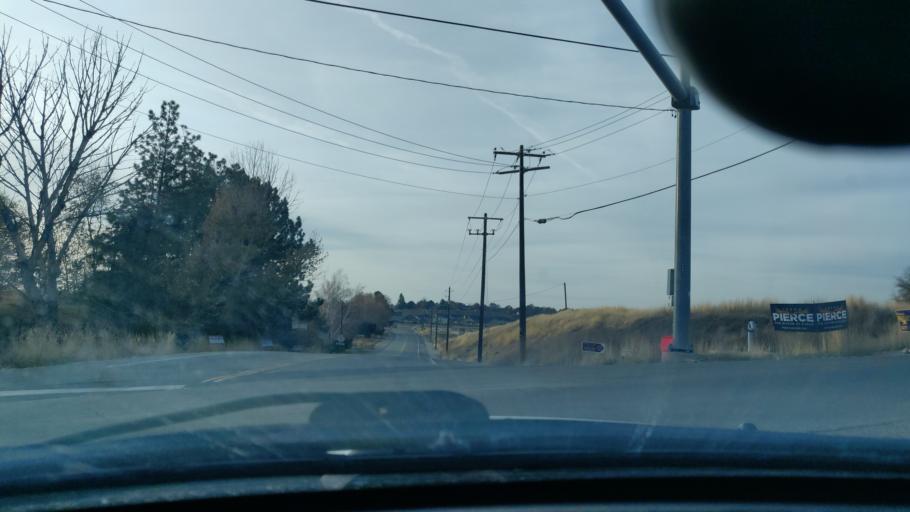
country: US
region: Idaho
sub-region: Ada County
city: Eagle
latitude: 43.6923
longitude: -116.3139
